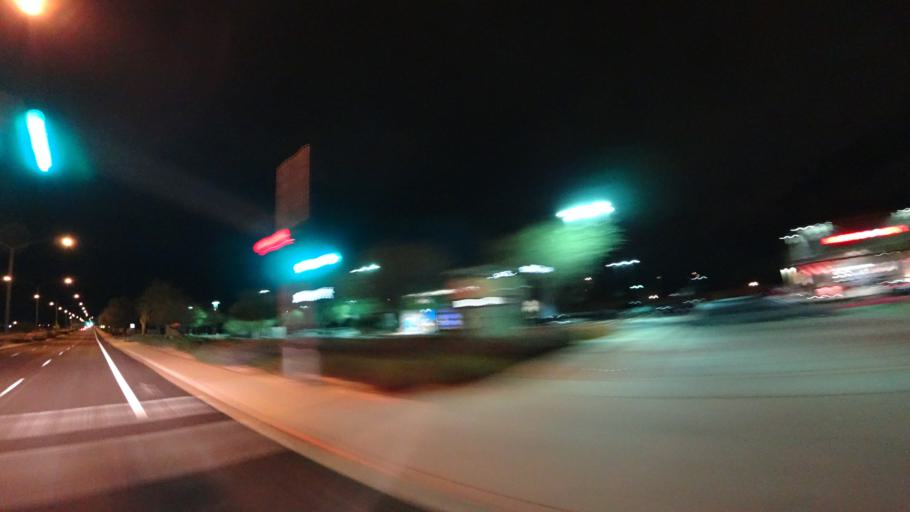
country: US
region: Arizona
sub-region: Pinal County
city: Apache Junction
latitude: 33.3788
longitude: -111.5993
